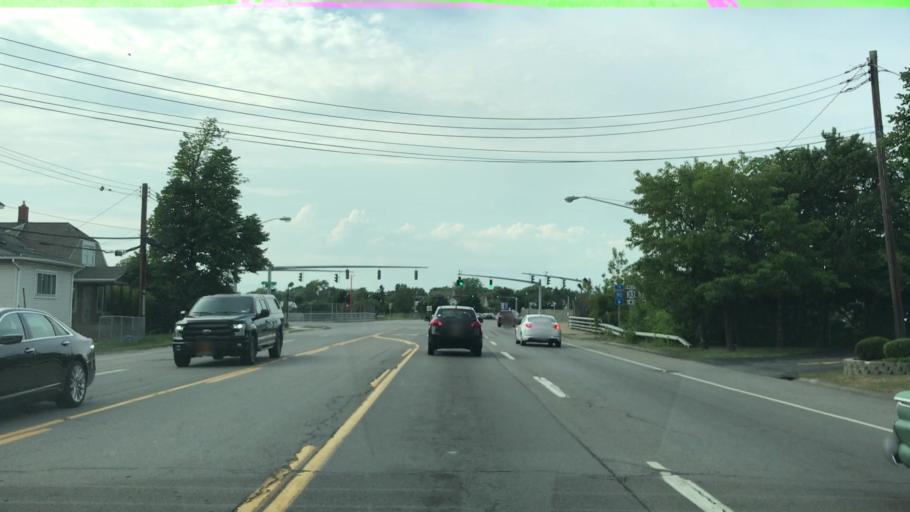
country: US
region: New York
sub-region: Erie County
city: Cheektowaga
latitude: 42.9282
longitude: -78.7434
